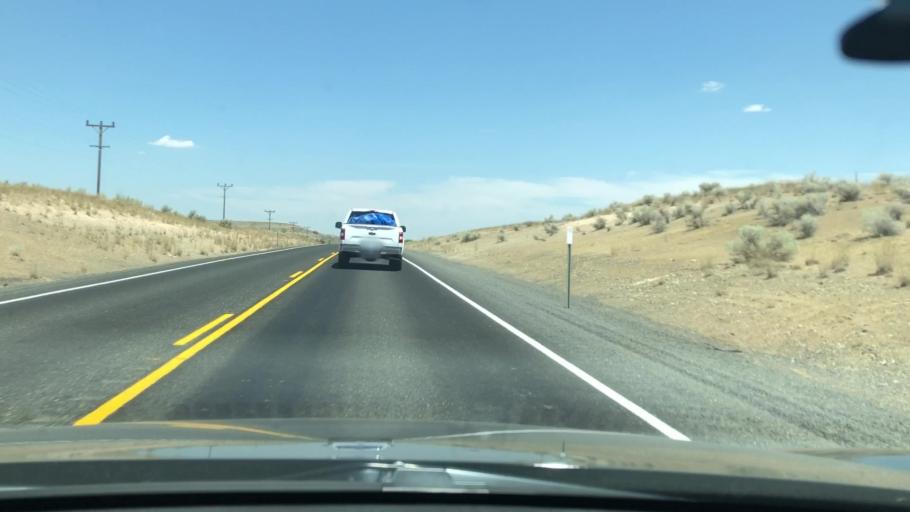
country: US
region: Idaho
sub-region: Owyhee County
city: Marsing
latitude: 43.0939
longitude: -117.0622
